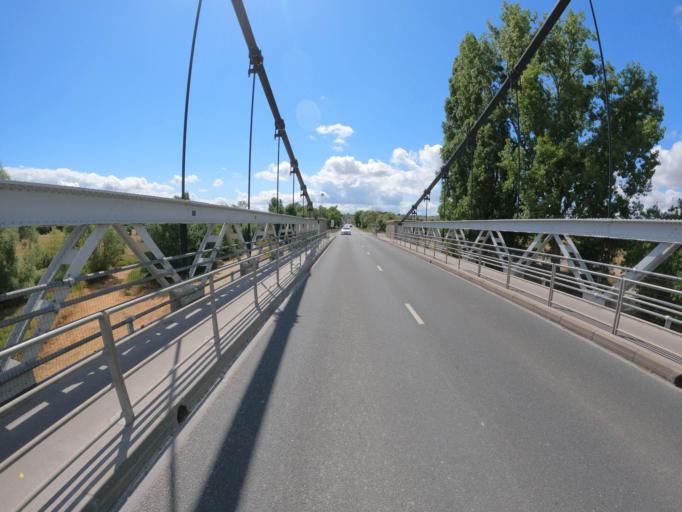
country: FR
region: Pays de la Loire
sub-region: Departement de la Loire-Atlantique
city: Ancenis
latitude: 47.3603
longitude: -1.1756
